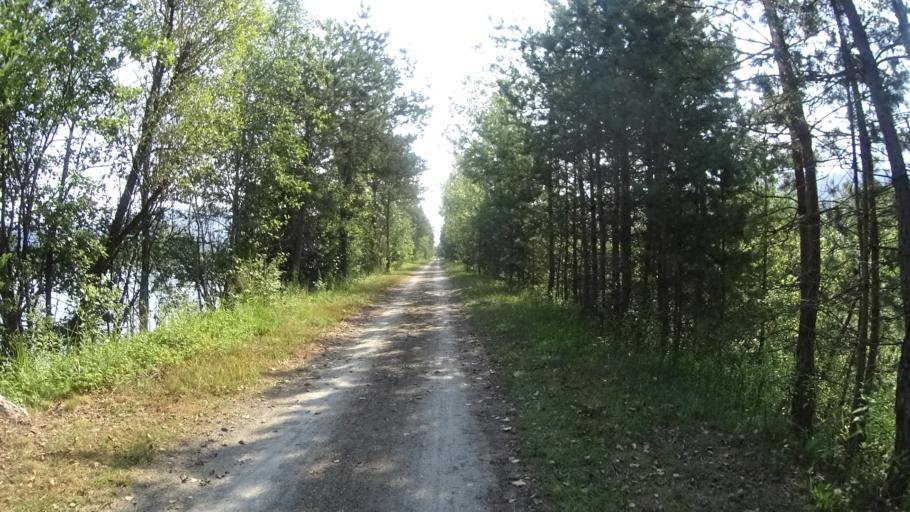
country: AT
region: Carinthia
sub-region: Politischer Bezirk Klagenfurt Land
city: Ebenthal
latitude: 46.5544
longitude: 14.4033
